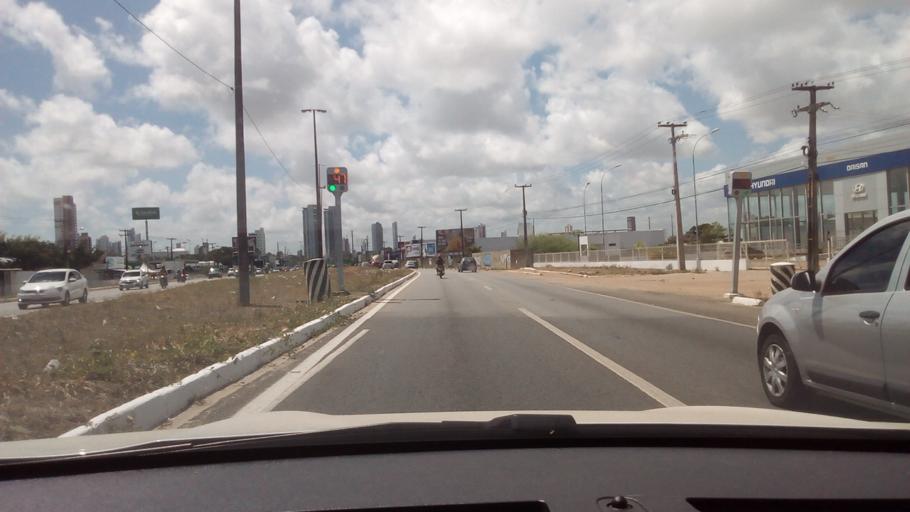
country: BR
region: Paraiba
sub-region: Joao Pessoa
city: Joao Pessoa
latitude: -7.0875
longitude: -34.8486
